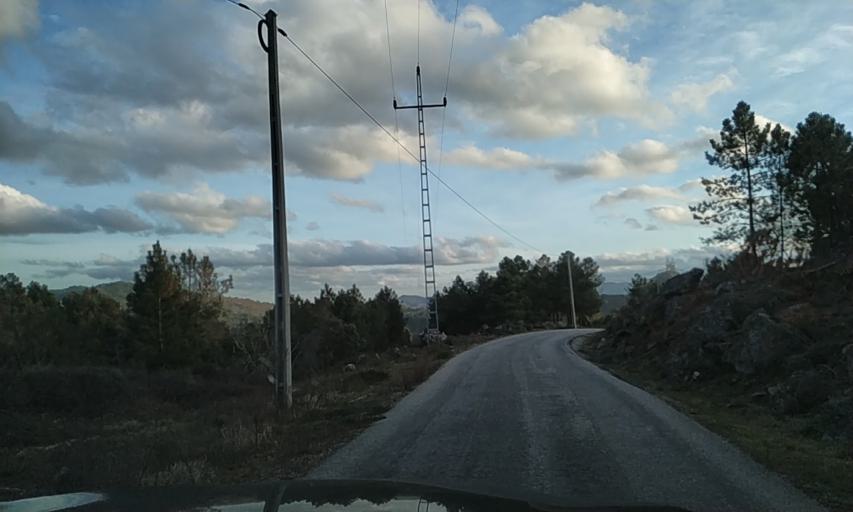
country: PT
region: Braganca
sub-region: Carrazeda de Ansiaes
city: Carrazeda de Anciaes
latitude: 41.2192
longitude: -7.3626
